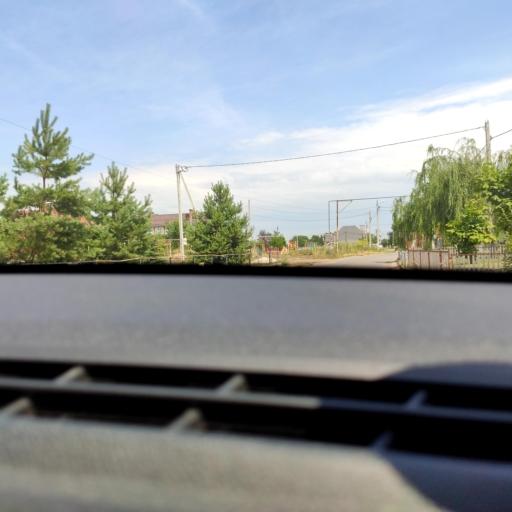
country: RU
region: Samara
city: Podstepki
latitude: 53.5117
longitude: 49.2264
